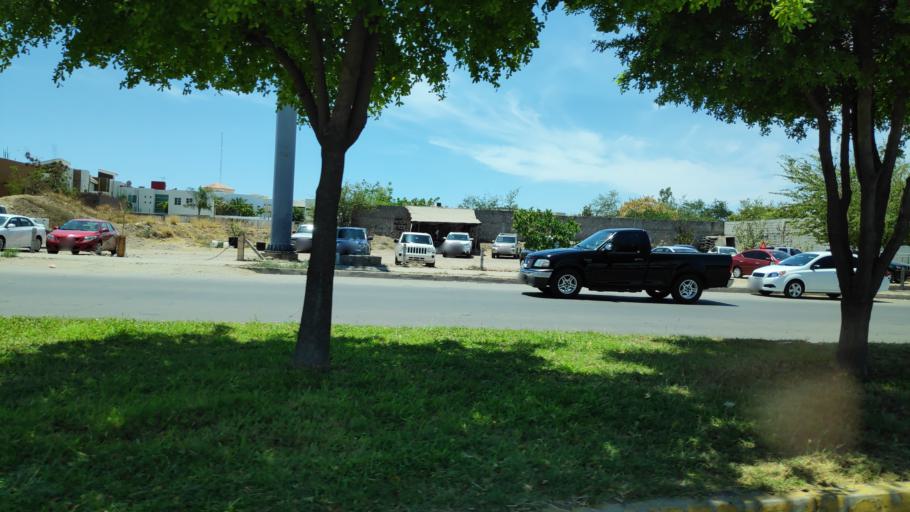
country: MX
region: Sinaloa
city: Culiacan
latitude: 24.8288
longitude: -107.3995
